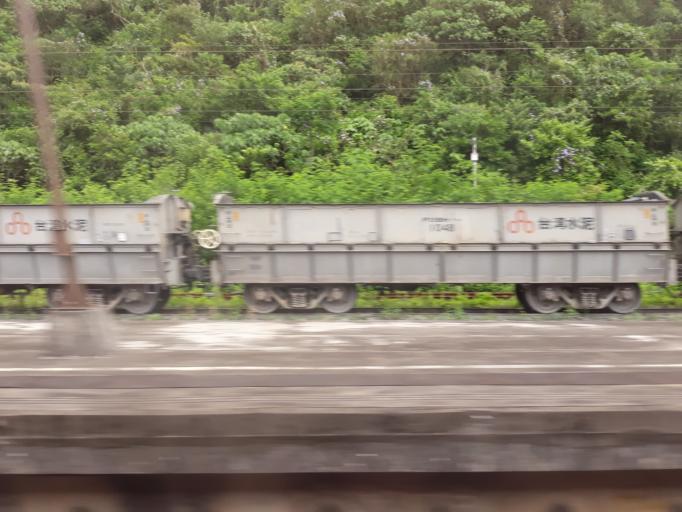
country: TW
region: Taiwan
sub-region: Yilan
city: Yilan
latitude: 24.5692
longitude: 121.8447
